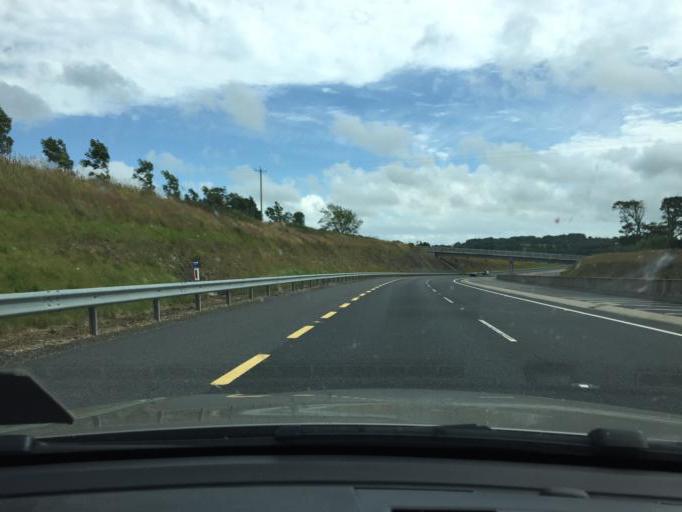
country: IE
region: Leinster
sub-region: Kilkenny
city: Mooncoin
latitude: 52.2455
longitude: -7.1896
